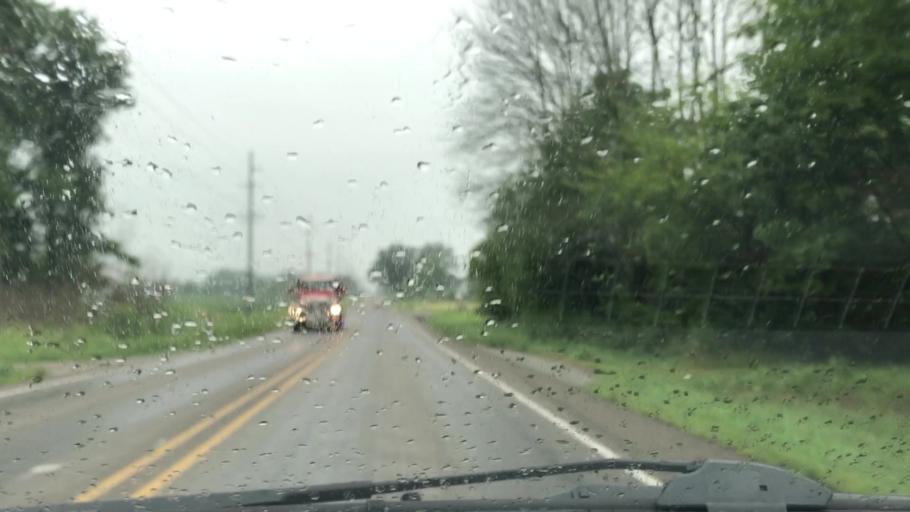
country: US
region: Indiana
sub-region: Hamilton County
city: Westfield
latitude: 40.1020
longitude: -86.1459
